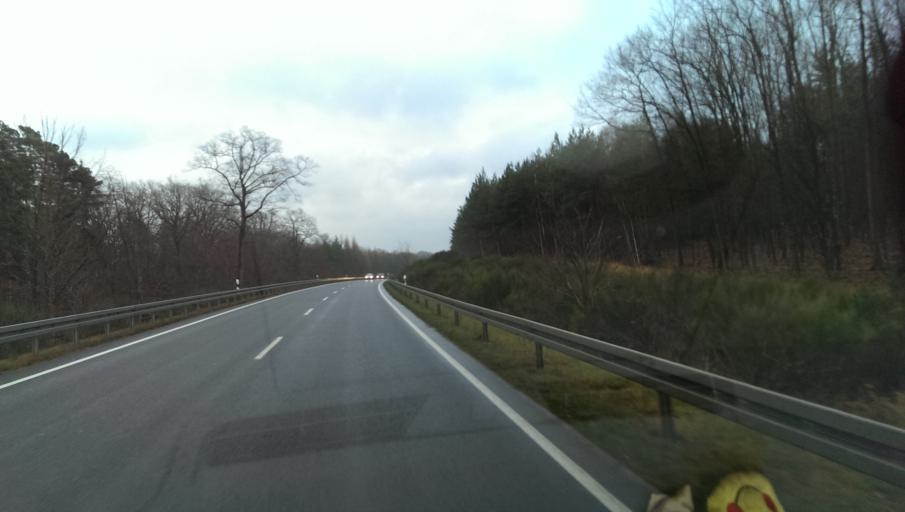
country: DE
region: Saxony
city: Moritzburg
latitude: 51.1566
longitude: 13.6386
